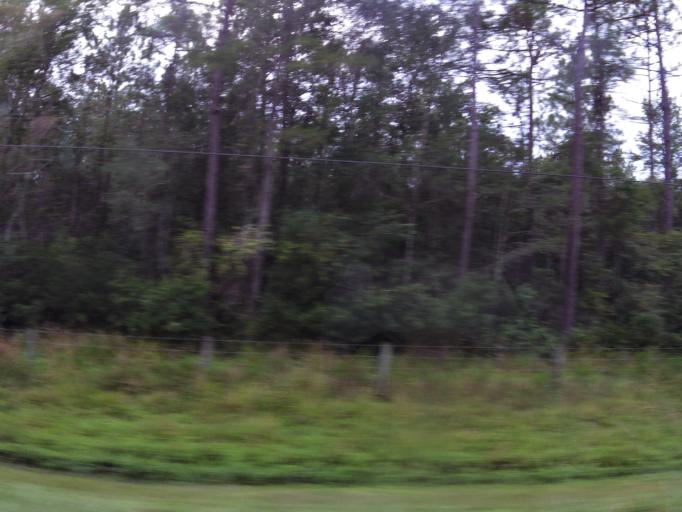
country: US
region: Florida
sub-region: Duval County
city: Baldwin
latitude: 30.3564
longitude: -81.9151
